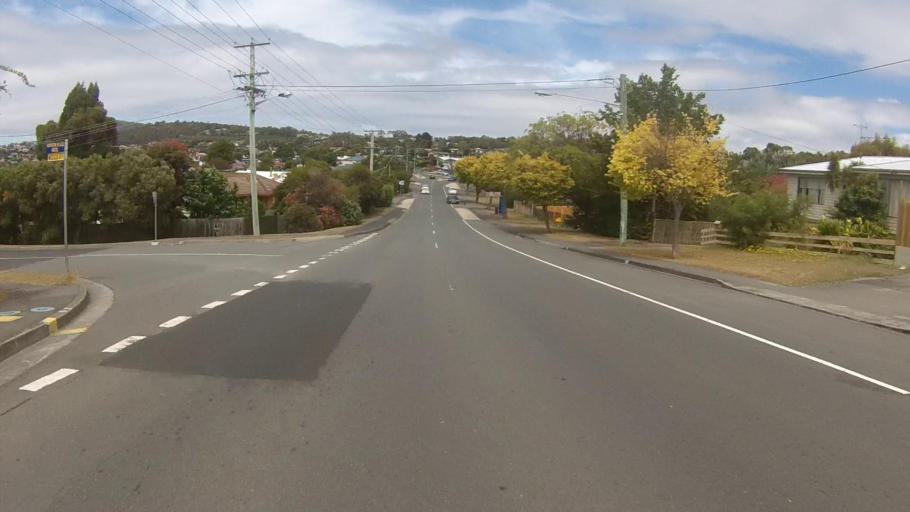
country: AU
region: Tasmania
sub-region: Kingborough
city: Blackmans Bay
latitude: -42.9978
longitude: 147.3222
